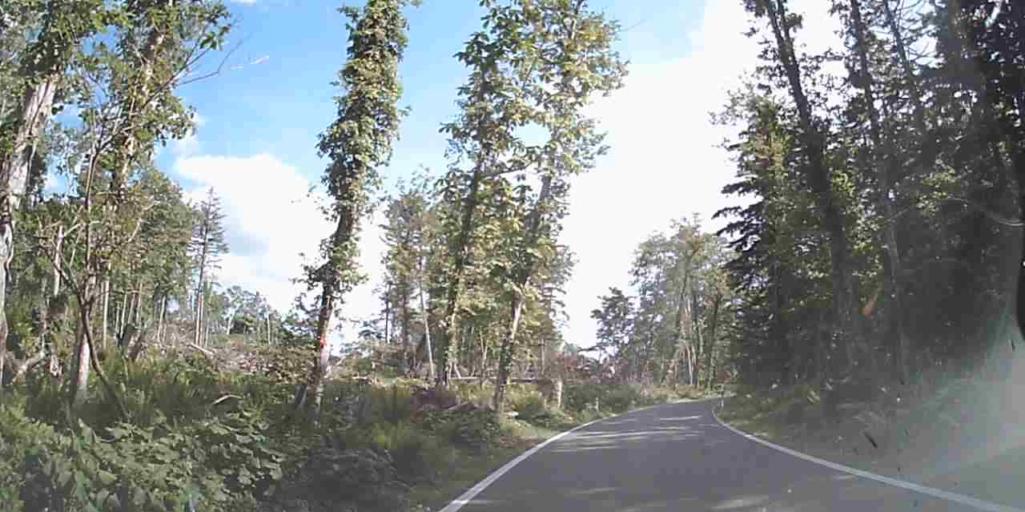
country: JP
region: Hokkaido
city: Shiraoi
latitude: 42.7255
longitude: 141.4137
